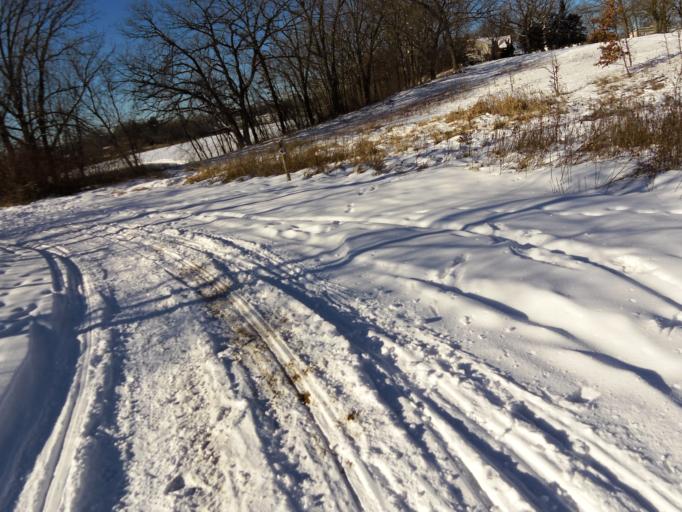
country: US
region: Minnesota
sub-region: Washington County
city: Lake Elmo
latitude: 44.9927
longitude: -92.9126
